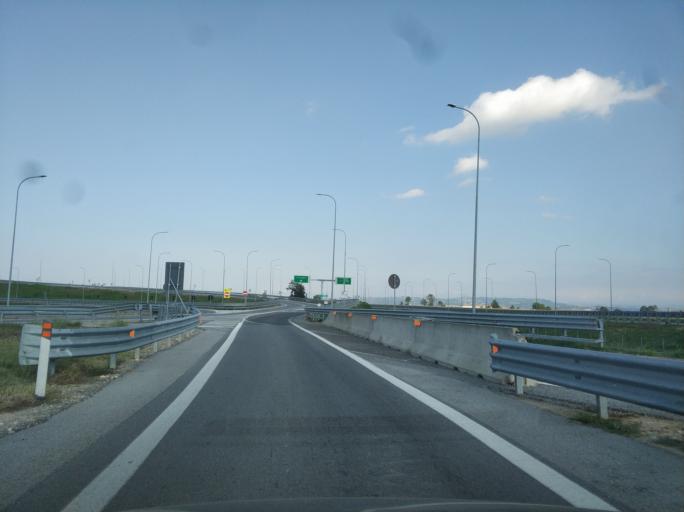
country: IT
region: Piedmont
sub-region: Provincia di Cuneo
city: Roreto
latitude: 44.6634
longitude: 7.8049
